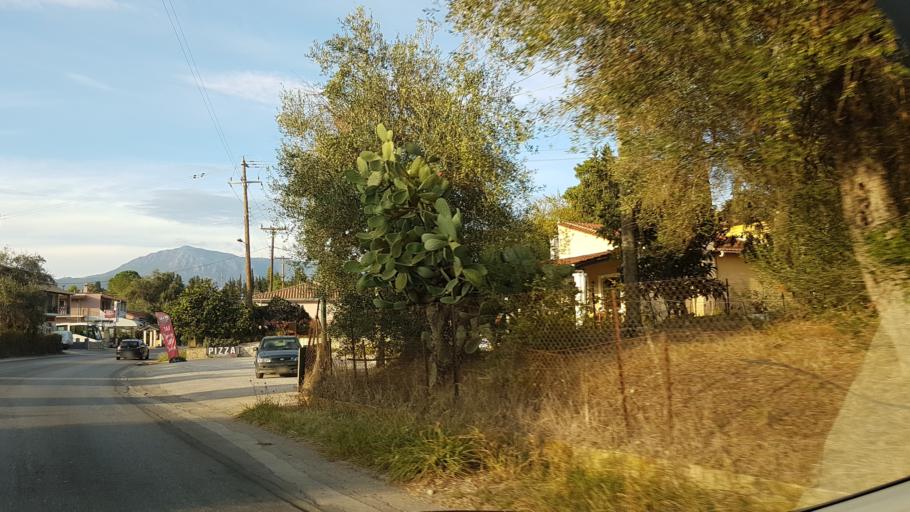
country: GR
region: Ionian Islands
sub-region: Nomos Kerkyras
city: Kontokali
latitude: 39.6659
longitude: 19.8435
